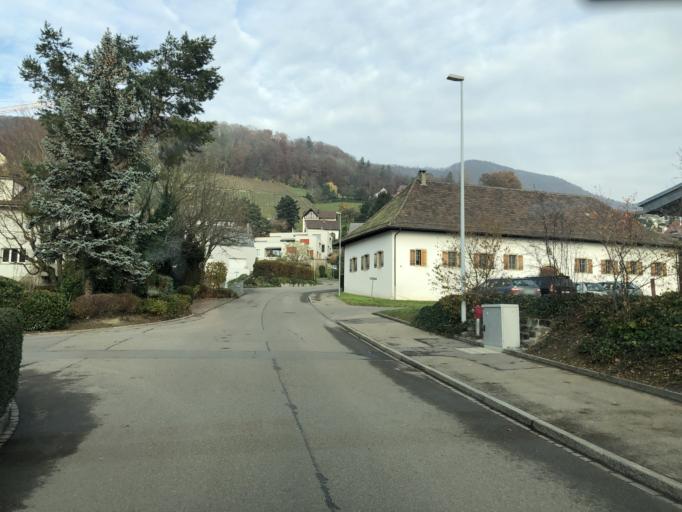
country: CH
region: Aargau
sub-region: Bezirk Baden
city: Wettingen
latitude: 47.4687
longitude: 8.3329
